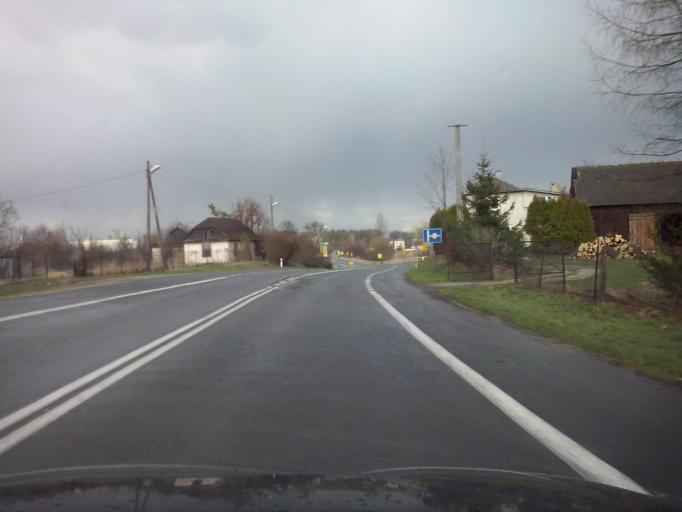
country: PL
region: Lublin Voivodeship
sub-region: Powiat krasnostawski
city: Krasnystaw
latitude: 51.0115
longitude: 23.1905
